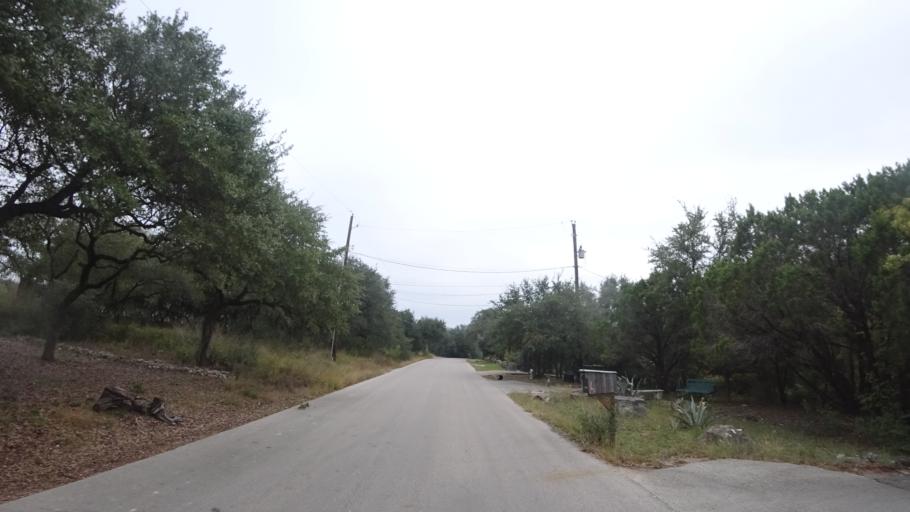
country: US
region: Texas
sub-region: Travis County
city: Hudson Bend
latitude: 30.3704
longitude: -97.9226
